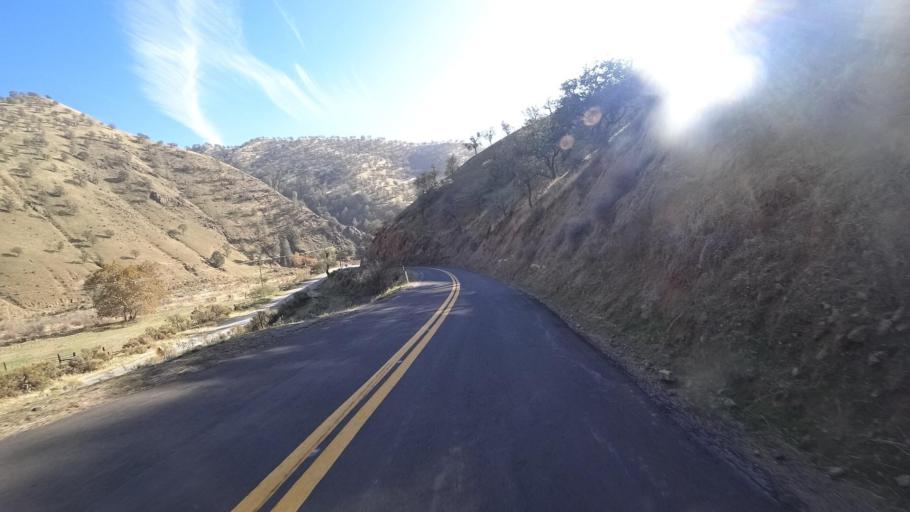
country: US
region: California
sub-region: Kern County
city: Bear Valley Springs
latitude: 35.3064
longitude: -118.5847
